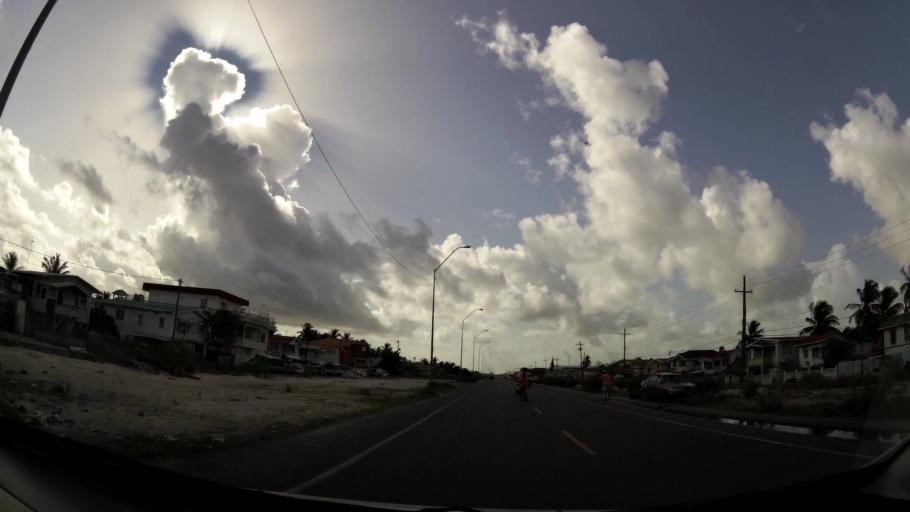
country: GY
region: Demerara-Mahaica
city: Georgetown
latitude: 6.8055
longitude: -58.0505
